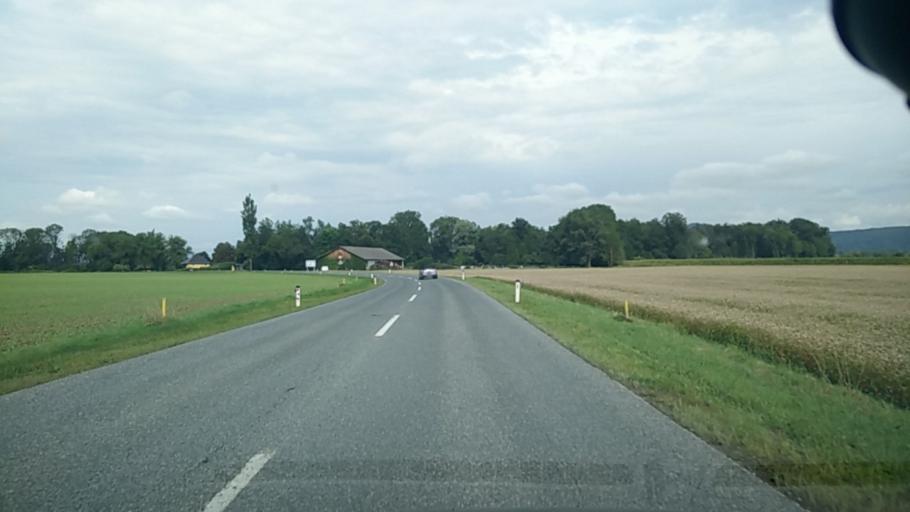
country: AT
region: Carinthia
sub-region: Politischer Bezirk Klagenfurt Land
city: Poggersdorf
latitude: 46.6280
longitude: 14.4239
